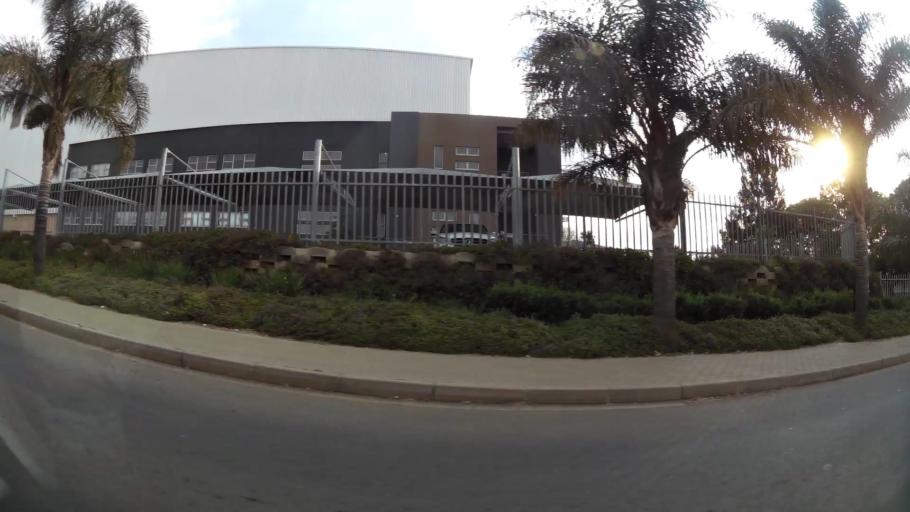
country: ZA
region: Gauteng
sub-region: City of Johannesburg Metropolitan Municipality
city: Modderfontein
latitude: -26.1571
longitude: 28.1889
